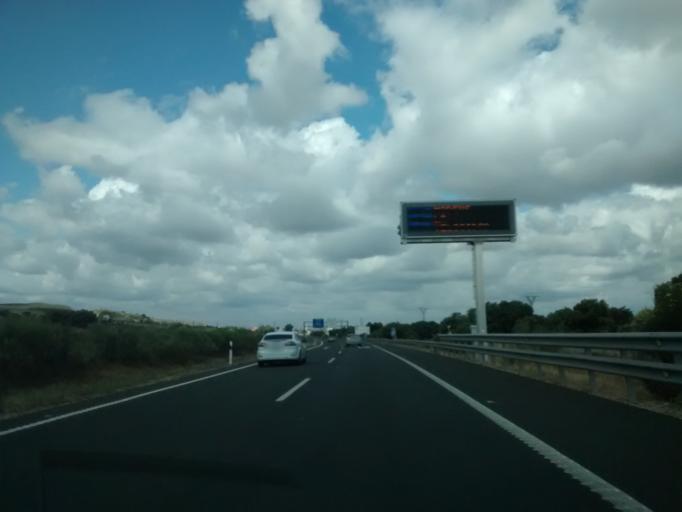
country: ES
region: Extremadura
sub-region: Provincia de Caceres
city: Navalmoral de la Mata
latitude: 39.8898
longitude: -5.5029
